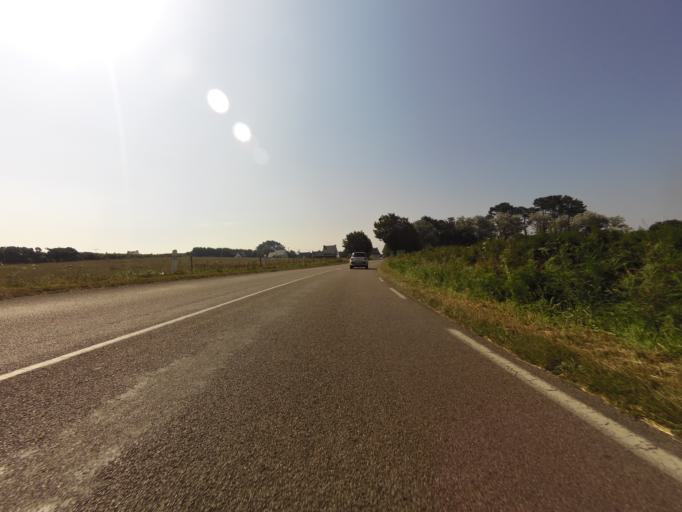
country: FR
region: Brittany
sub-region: Departement du Finistere
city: Plozevet
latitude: 47.9960
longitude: -4.4365
